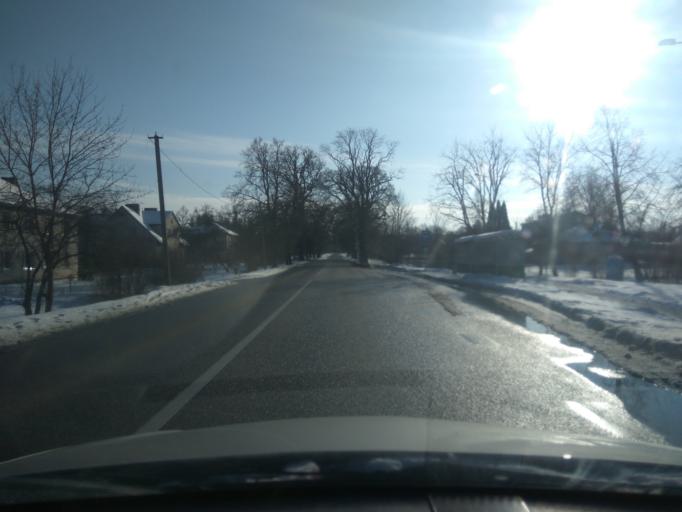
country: LV
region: Kuldigas Rajons
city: Kuldiga
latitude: 57.2788
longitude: 22.0221
